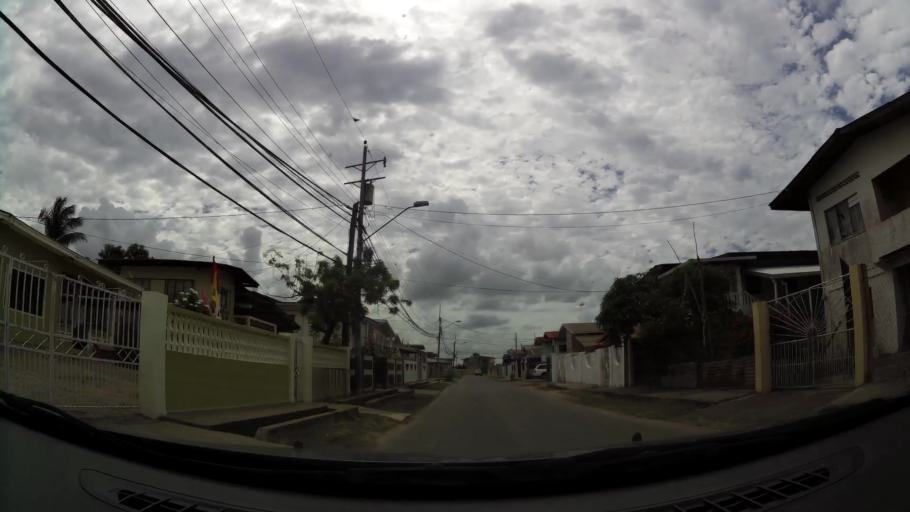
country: TT
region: Couva-Tabaquite-Talparo
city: Couva
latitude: 10.3993
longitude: -61.4679
